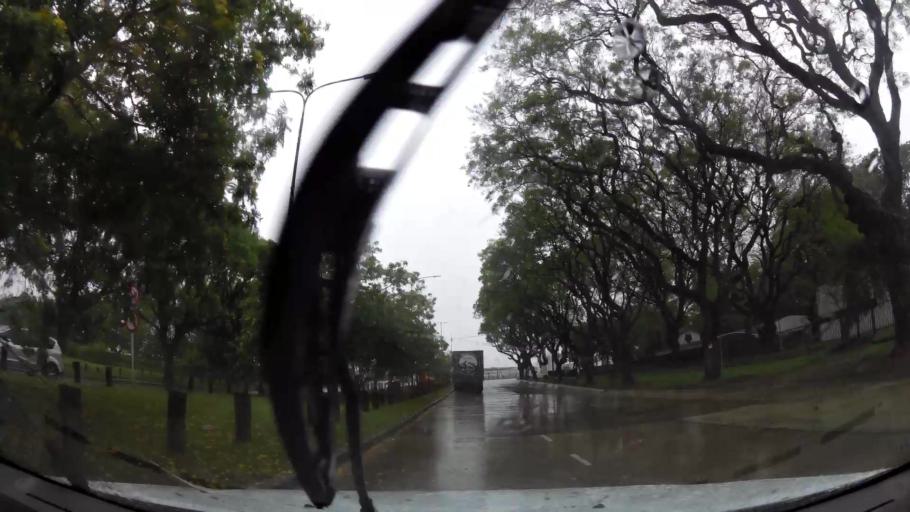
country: AR
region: Buenos Aires F.D.
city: Colegiales
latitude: -34.5634
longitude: -58.4176
